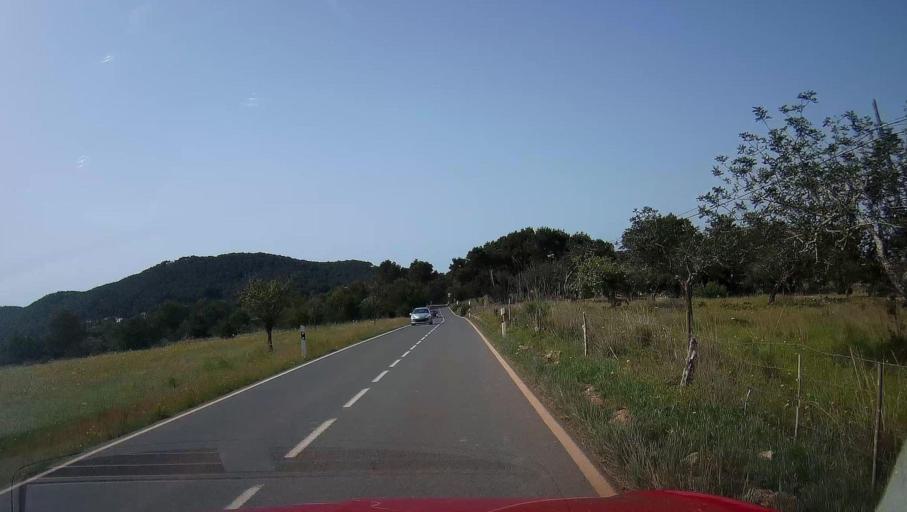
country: ES
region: Balearic Islands
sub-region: Illes Balears
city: Sant Joan de Labritja
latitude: 39.0491
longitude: 1.5715
